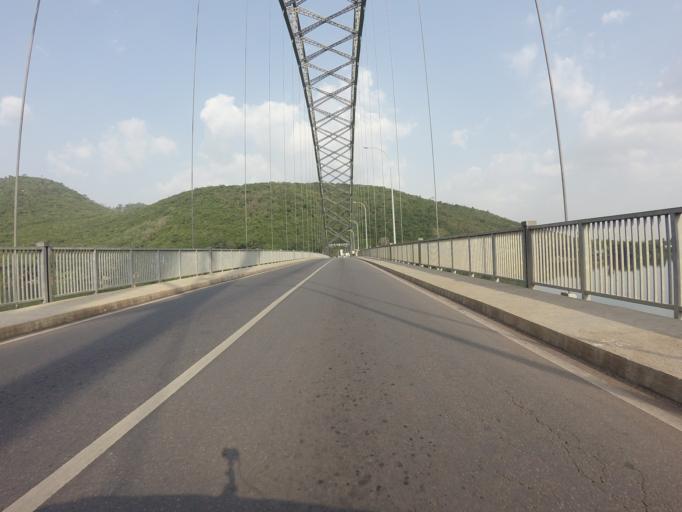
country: GH
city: Akropong
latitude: 6.2397
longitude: 0.0948
